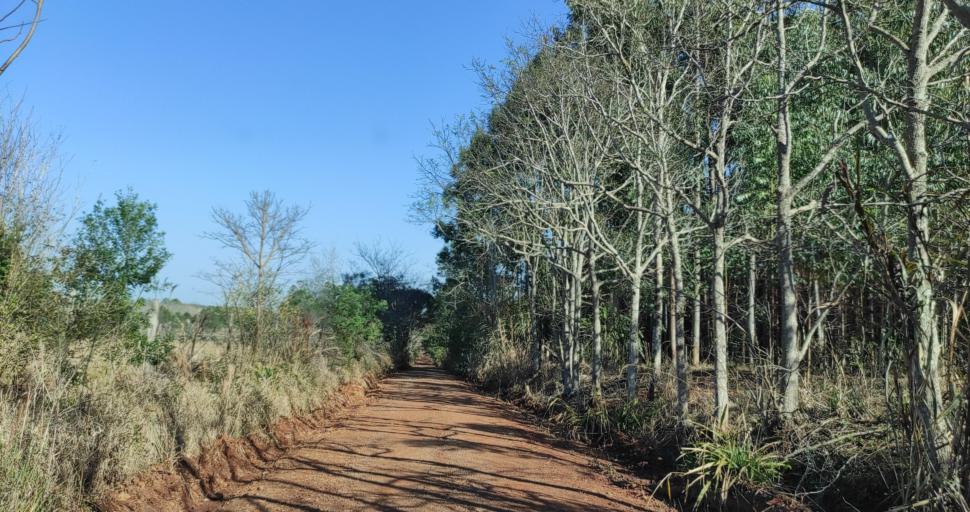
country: AR
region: Misiones
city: Capiovi
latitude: -26.8938
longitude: -55.0389
